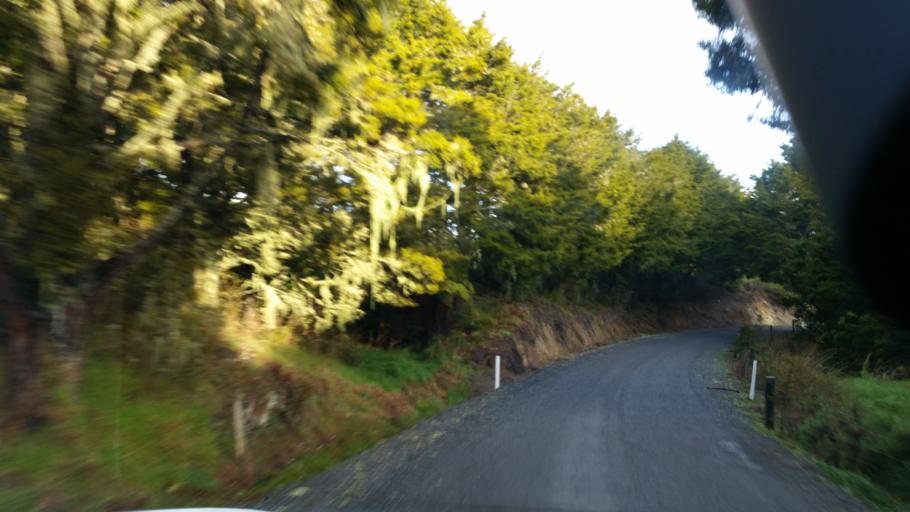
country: NZ
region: Northland
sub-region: Whangarei
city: Maungatapere
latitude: -35.7794
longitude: 174.0922
